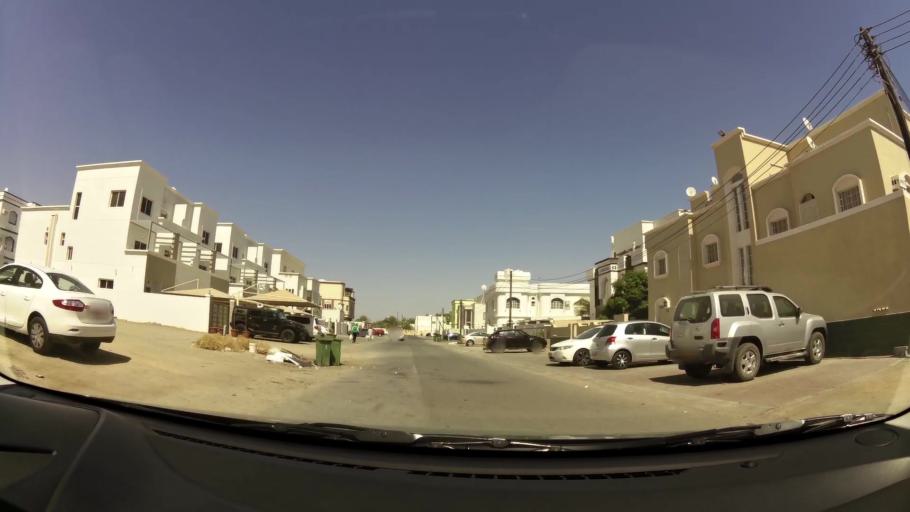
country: OM
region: Muhafazat Masqat
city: As Sib al Jadidah
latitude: 23.6015
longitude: 58.2468
